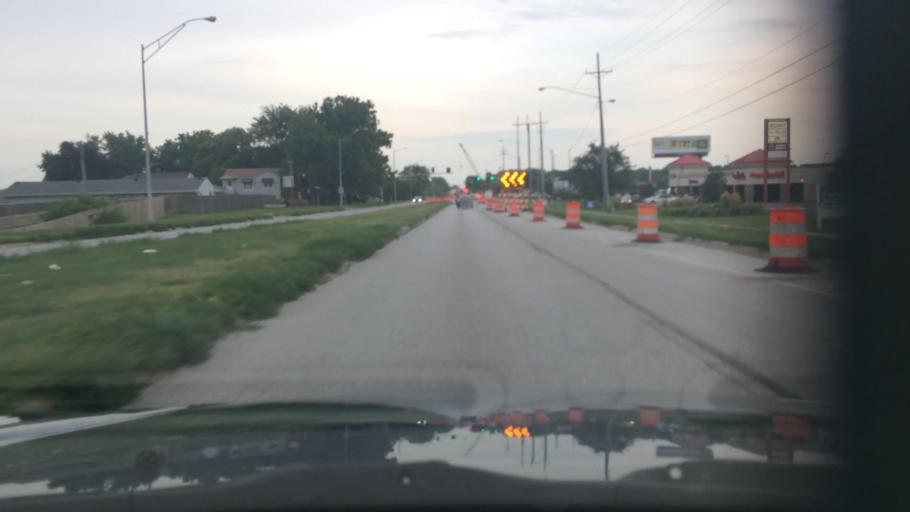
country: US
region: Nebraska
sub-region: Douglas County
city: Ralston
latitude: 41.2026
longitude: -96.0431
